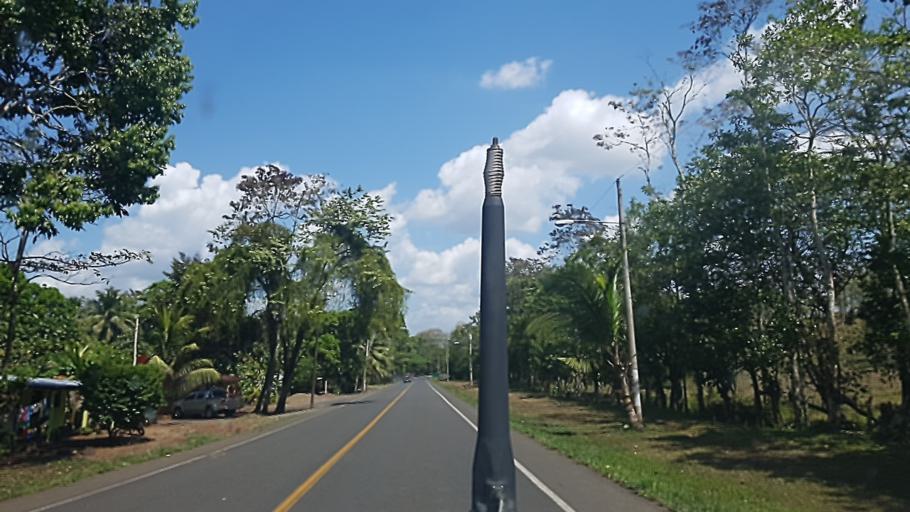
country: NI
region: Atlantico Sur
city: Muelle de los Bueyes
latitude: 11.9117
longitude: -84.6409
